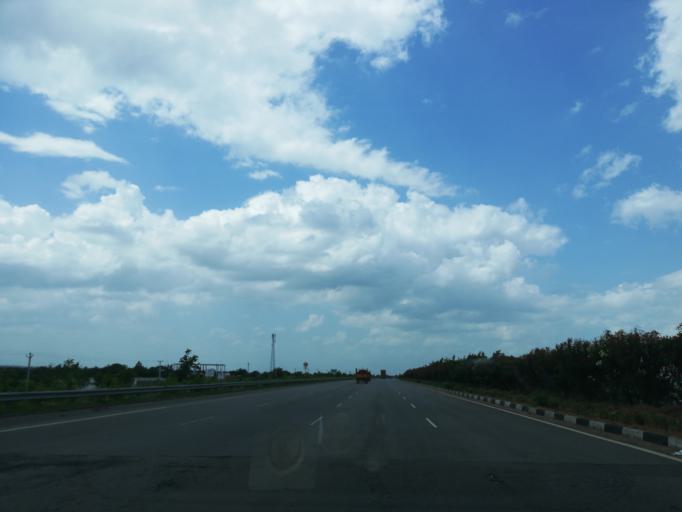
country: IN
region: Telangana
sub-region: Medak
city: Patancheru
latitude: 17.4848
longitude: 78.2461
